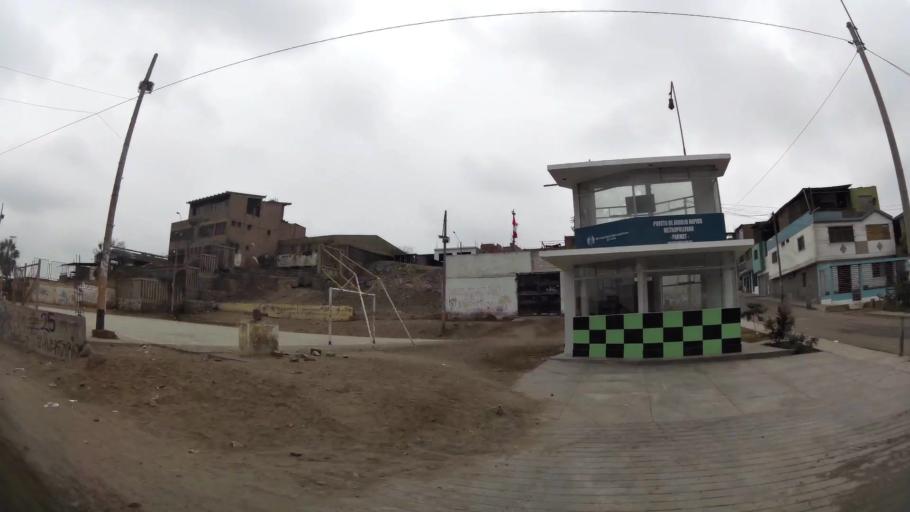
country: PE
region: Lima
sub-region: Lima
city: Surco
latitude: -12.1414
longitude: -76.9616
